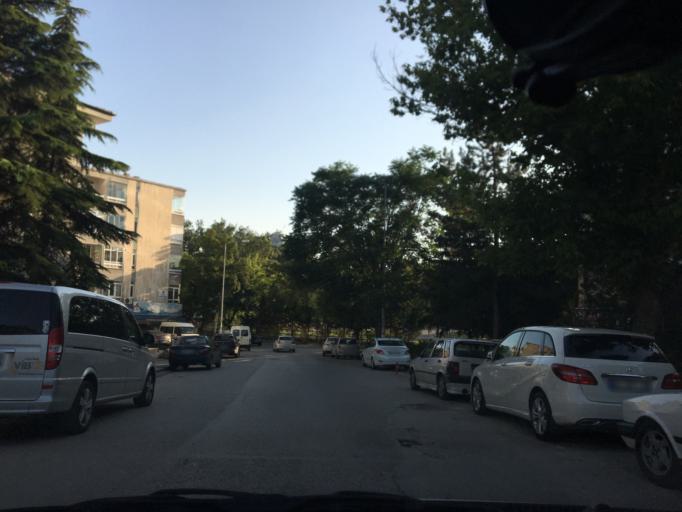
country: TR
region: Ankara
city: Ankara
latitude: 39.9072
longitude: 32.8536
